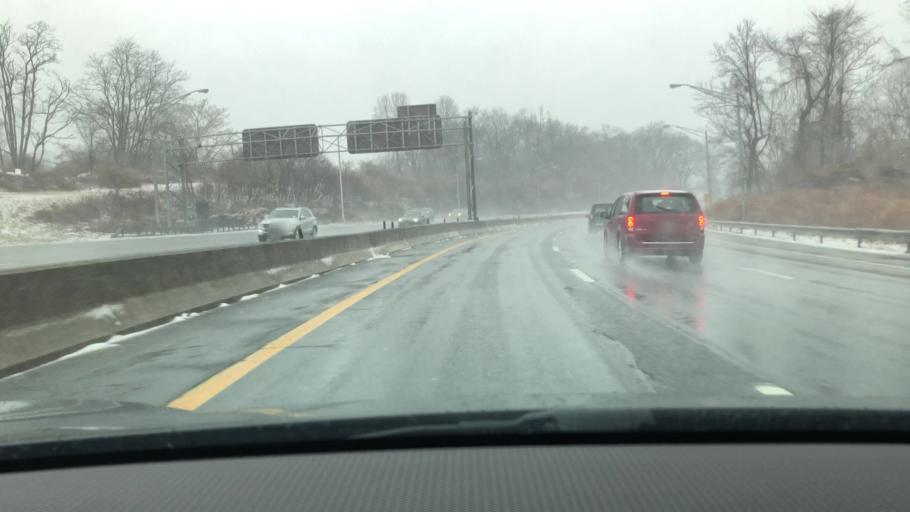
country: US
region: New York
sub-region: Westchester County
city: Tuckahoe
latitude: 40.9416
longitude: -73.8048
